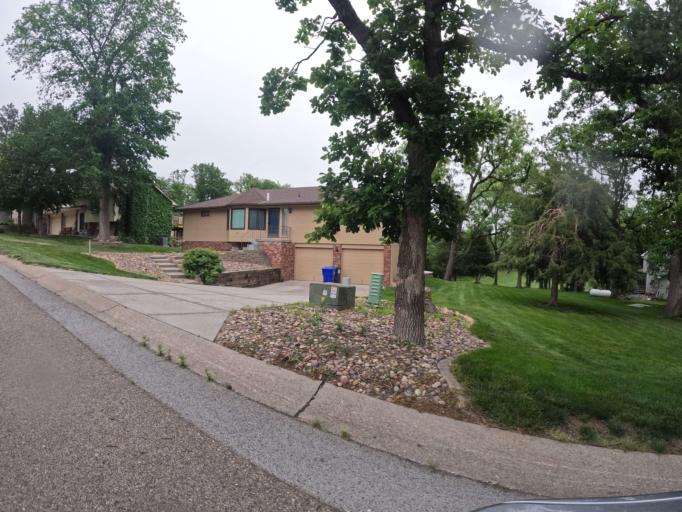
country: US
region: Nebraska
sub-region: Sarpy County
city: Offutt Air Force Base
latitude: 41.0460
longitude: -95.9709
